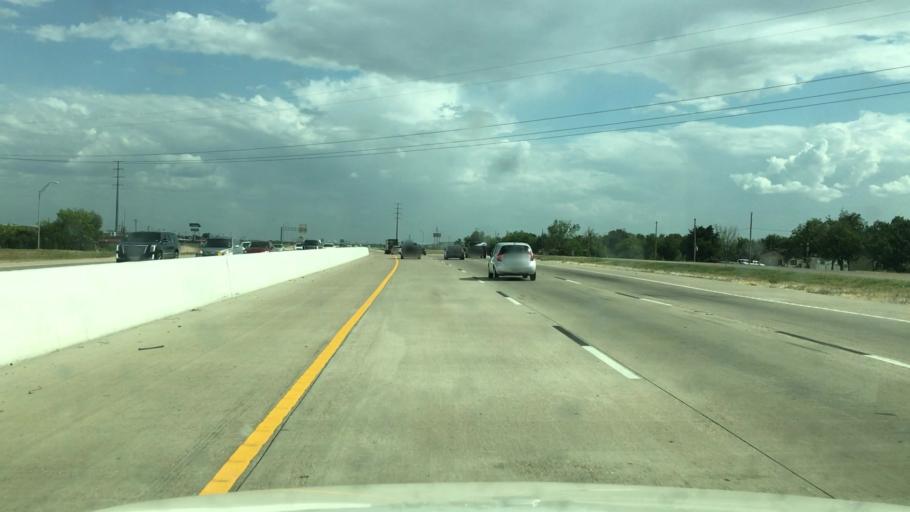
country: US
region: Texas
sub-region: McLennan County
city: Northcrest
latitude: 31.7007
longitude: -97.1023
